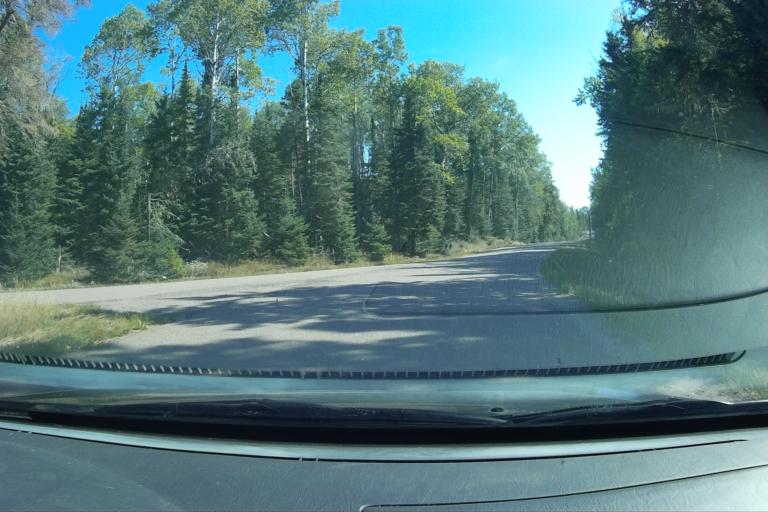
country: CA
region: Ontario
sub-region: Thunder Bay District
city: Thunder Bay
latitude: 48.3480
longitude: -88.8060
